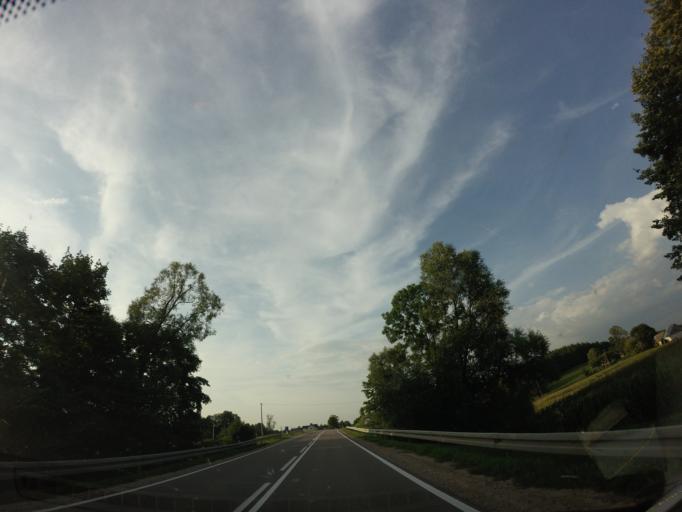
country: LT
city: Lazdijai
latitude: 54.1434
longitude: 23.4671
